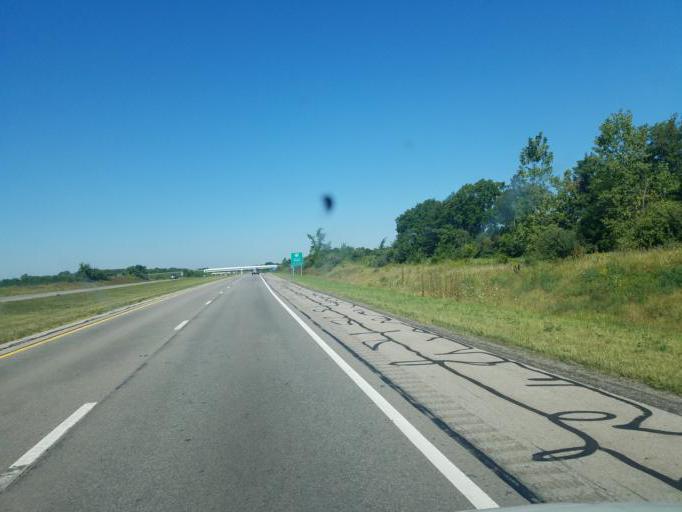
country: US
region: Ohio
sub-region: Crawford County
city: Galion
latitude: 40.7612
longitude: -82.7764
